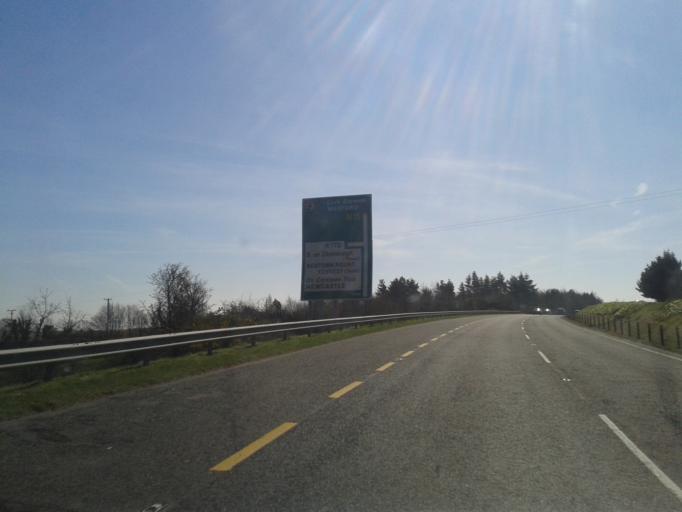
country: IE
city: Kilquade
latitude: 53.0864
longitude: -6.0909
